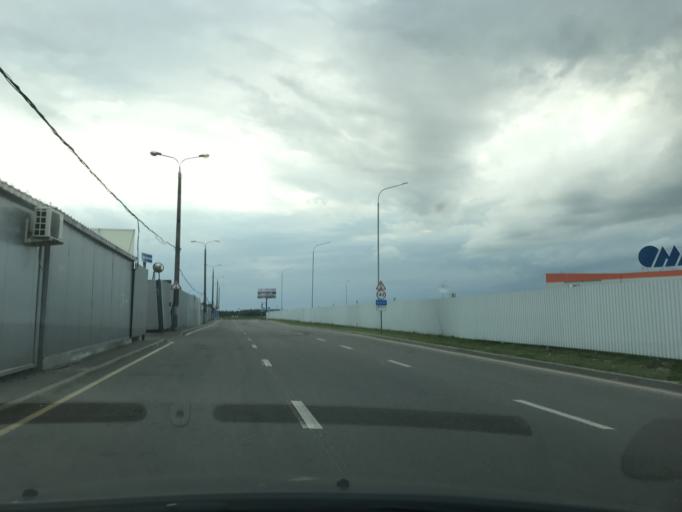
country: BY
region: Minsk
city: Borovlyany
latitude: 53.9655
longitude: 27.6255
